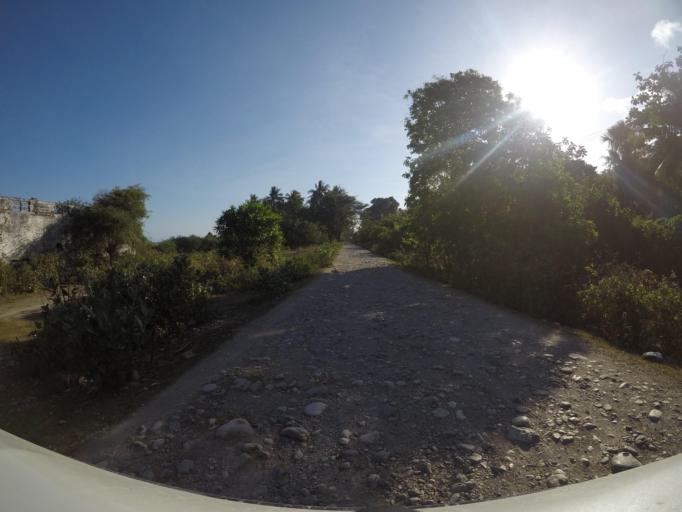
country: TL
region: Viqueque
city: Viqueque
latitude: -8.8018
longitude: 126.5861
